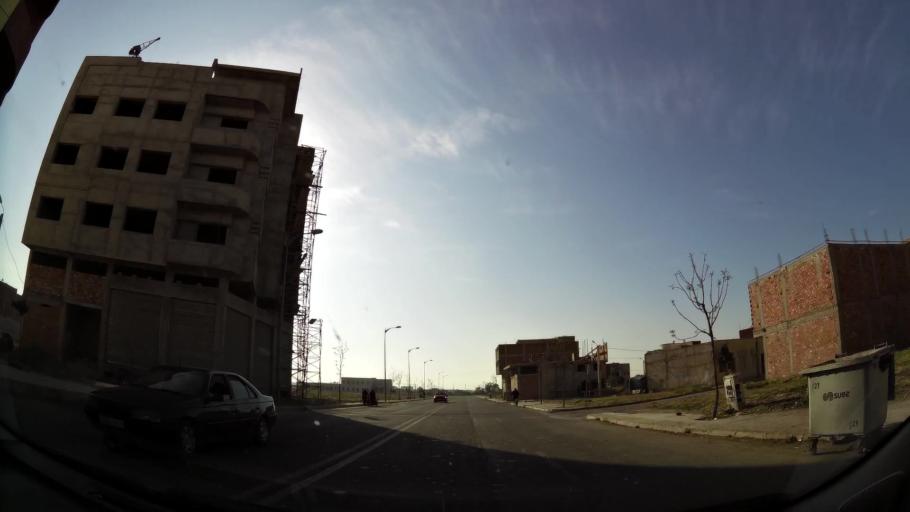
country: MA
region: Oriental
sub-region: Oujda-Angad
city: Oujda
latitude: 34.7184
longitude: -1.8984
